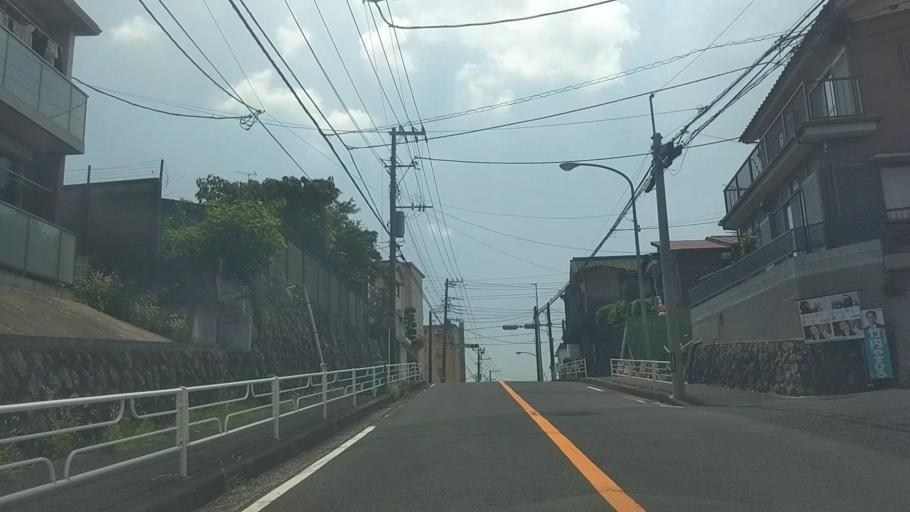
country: JP
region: Kanagawa
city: Yokohama
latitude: 35.4993
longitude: 139.6432
